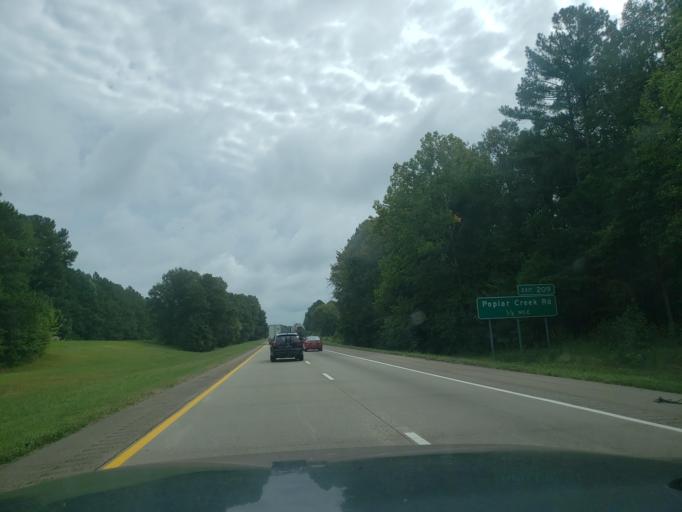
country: US
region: North Carolina
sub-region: Granville County
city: Oxford
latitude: 36.3211
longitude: -78.4987
